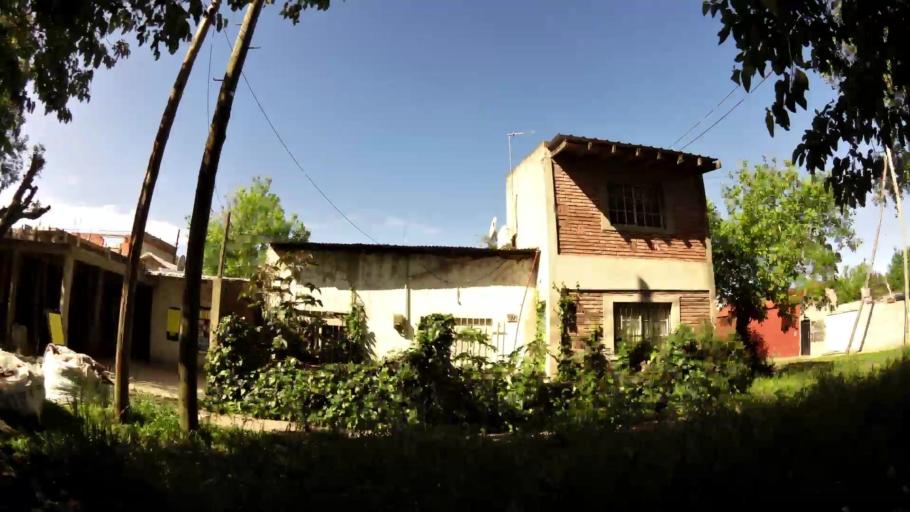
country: AR
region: Buenos Aires
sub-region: Partido de Quilmes
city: Quilmes
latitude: -34.8084
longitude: -58.2255
